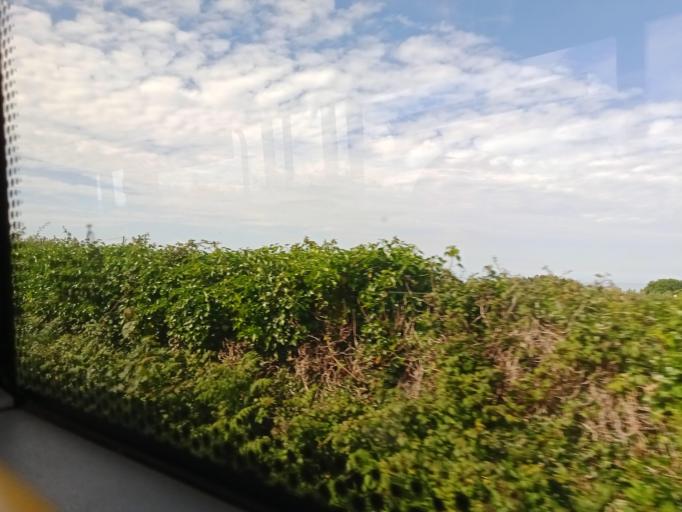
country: GB
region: Wales
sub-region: Anglesey
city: Llangoed
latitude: 53.3047
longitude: -4.0810
